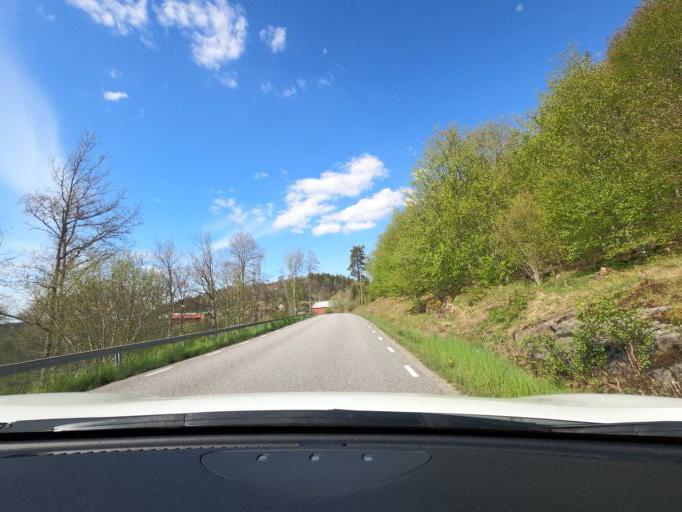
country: SE
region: Vaestra Goetaland
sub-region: Harryda Kommun
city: Ravlanda
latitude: 57.6330
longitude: 12.4981
